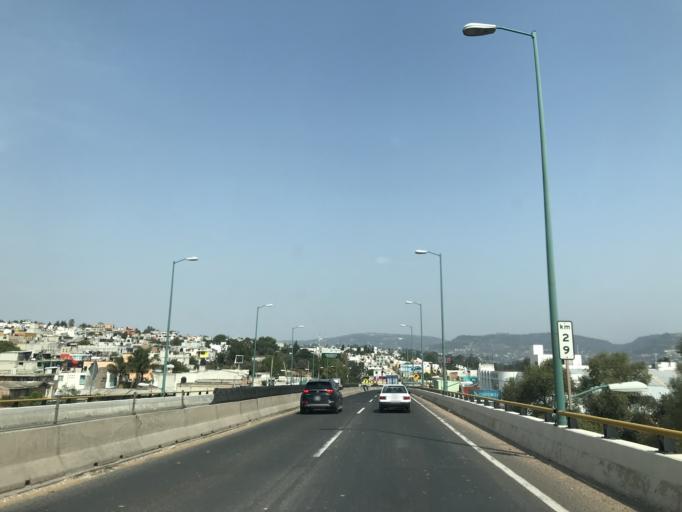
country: MX
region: Tlaxcala
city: Tlaxcala de Xicohtencatl
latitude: 19.3123
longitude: -98.2023
